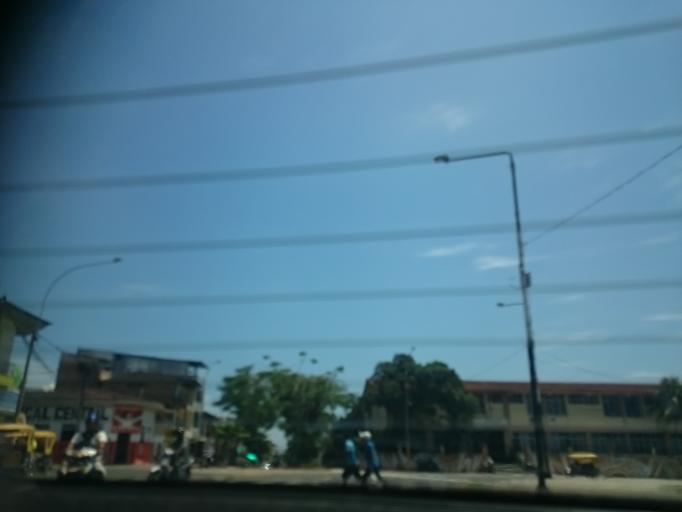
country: PE
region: Loreto
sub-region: Provincia de Maynas
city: Iquitos
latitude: -3.7551
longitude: -73.2499
